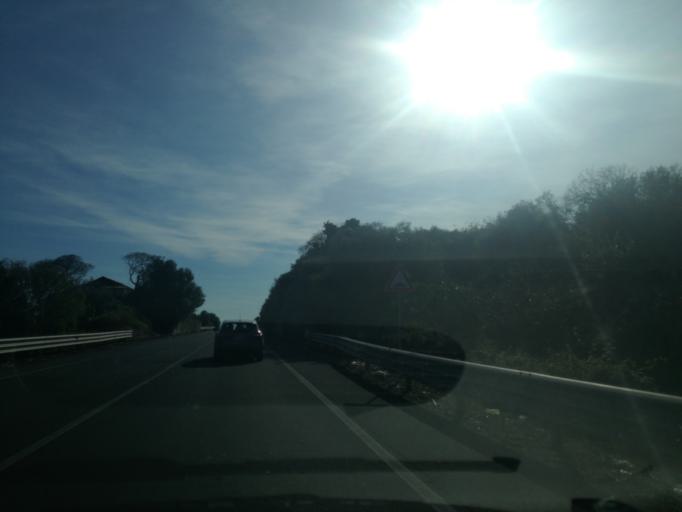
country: IT
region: Sicily
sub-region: Catania
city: Vambolieri
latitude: 37.5925
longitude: 15.1687
